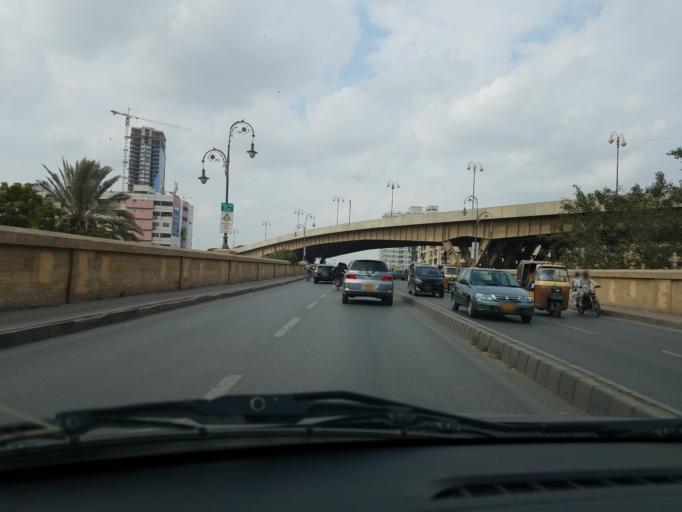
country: PK
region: Sindh
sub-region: Karachi District
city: Karachi
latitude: 24.8398
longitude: 67.0328
